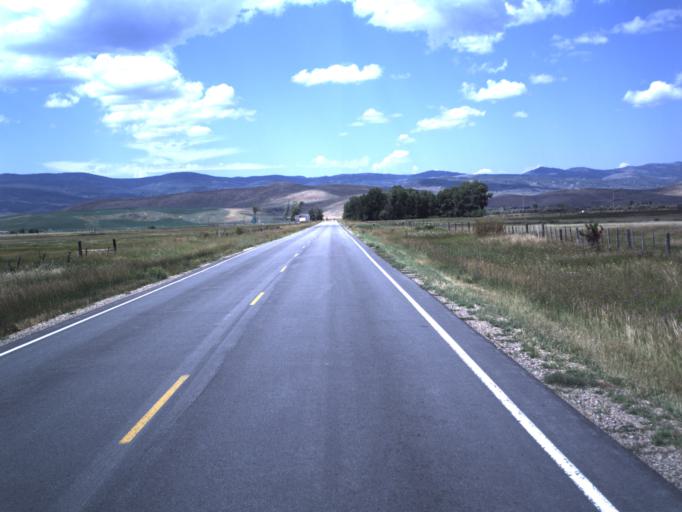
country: US
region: Utah
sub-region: Rich County
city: Randolph
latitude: 41.8363
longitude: -111.3337
